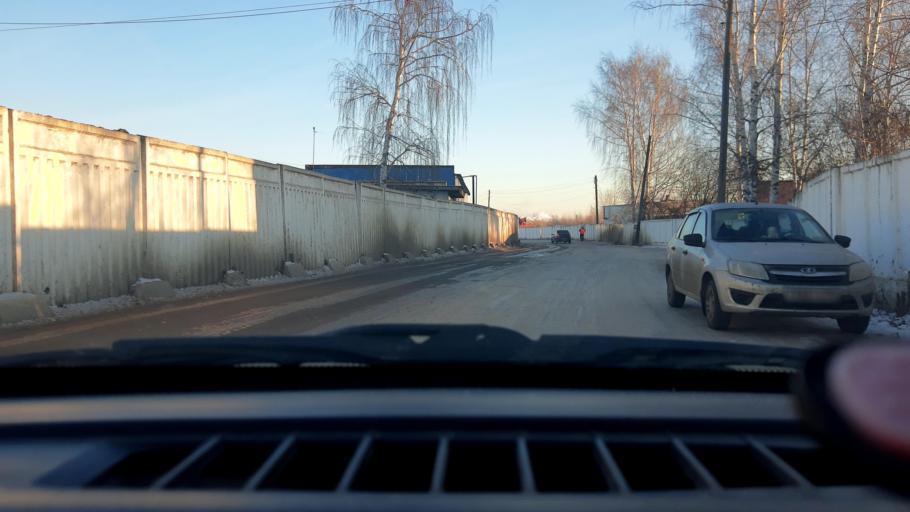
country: RU
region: Nizjnij Novgorod
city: Gorbatovka
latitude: 56.2785
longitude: 43.8401
